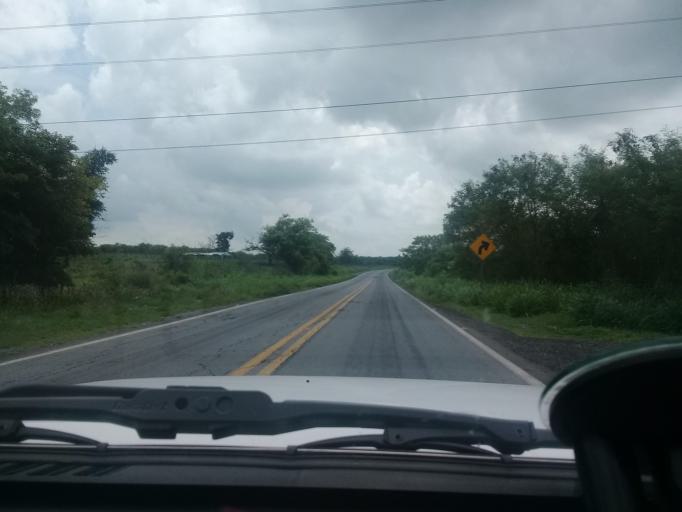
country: MX
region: Veracruz
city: Paso de Ovejas
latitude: 19.2919
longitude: -96.4570
